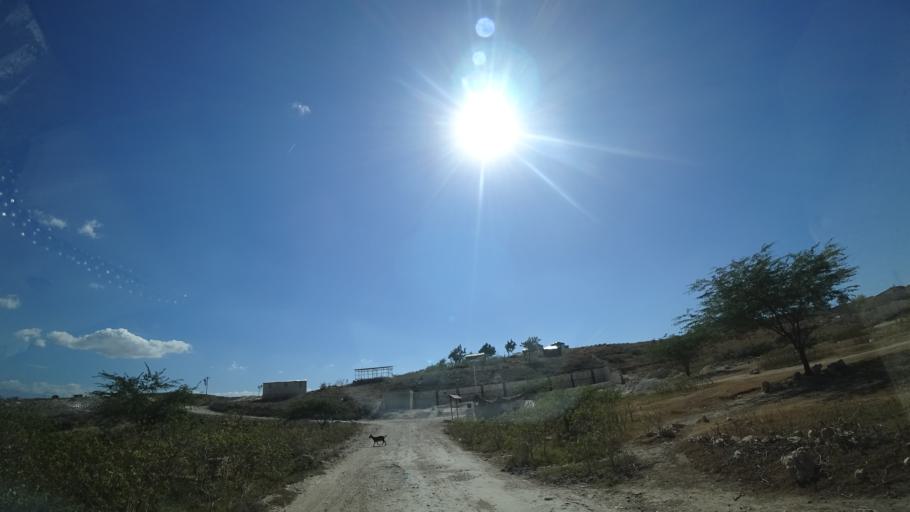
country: HT
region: Ouest
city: Cabaret
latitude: 18.6848
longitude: -72.3186
